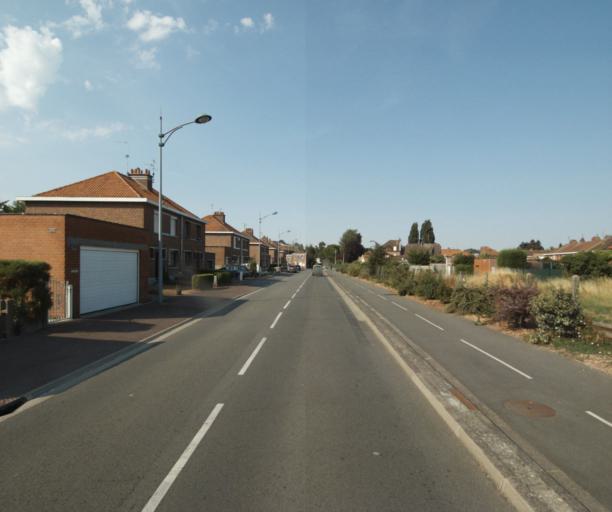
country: FR
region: Nord-Pas-de-Calais
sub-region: Departement du Nord
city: Comines
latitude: 50.7581
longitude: 3.0054
